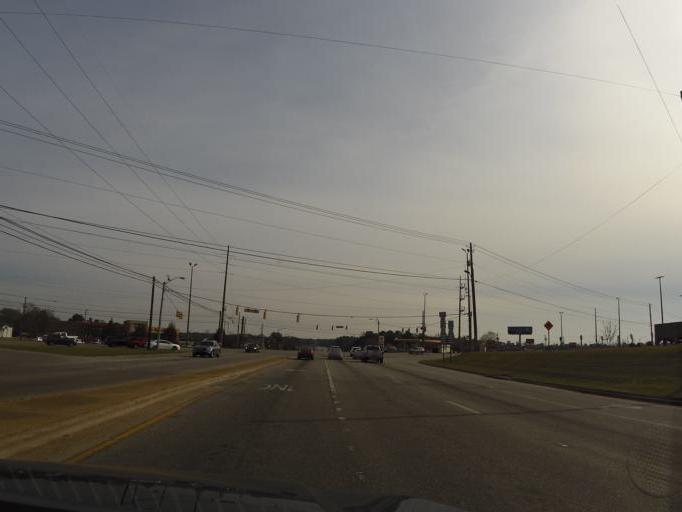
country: US
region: Alabama
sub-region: Houston County
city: Dothan
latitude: 31.2164
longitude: -85.3619
